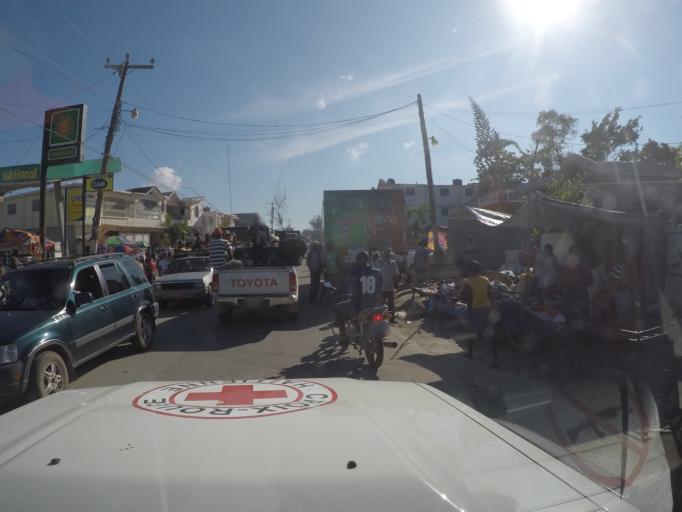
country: HT
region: Ouest
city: Grangwav
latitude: 18.4254
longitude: -72.7179
